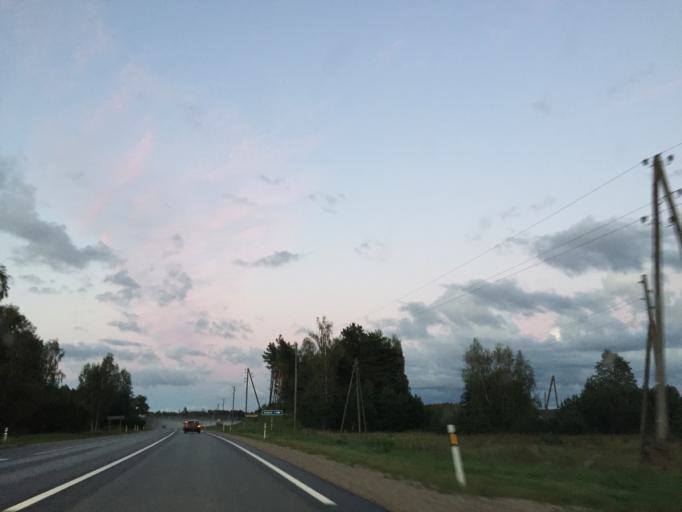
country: LV
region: Jurmala
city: Jurmala
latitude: 56.8974
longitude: 23.7318
